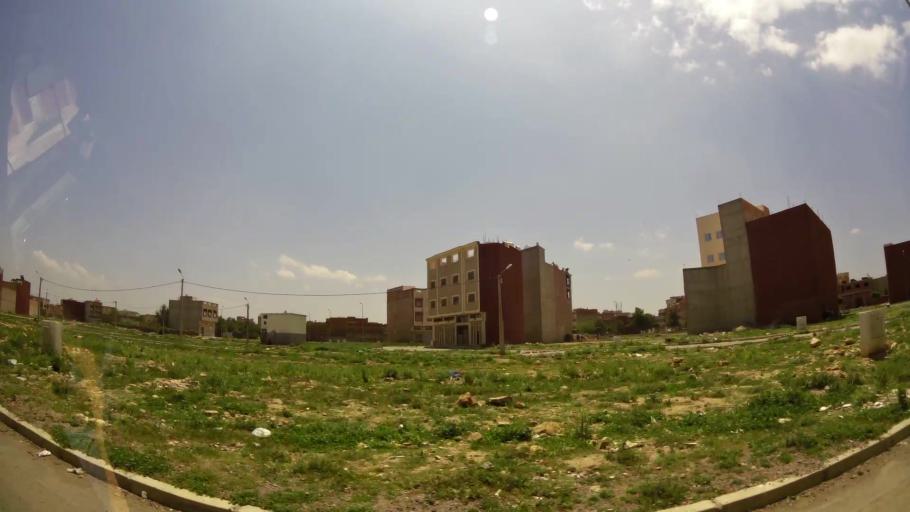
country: MA
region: Oriental
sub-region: Oujda-Angad
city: Oujda
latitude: 34.6928
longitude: -1.8911
